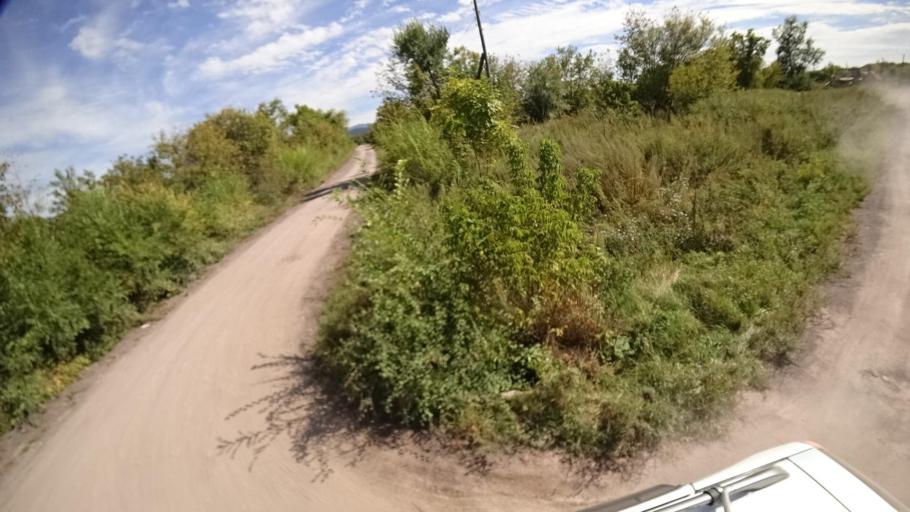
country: RU
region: Primorskiy
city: Yakovlevka
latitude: 44.4322
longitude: 133.5701
